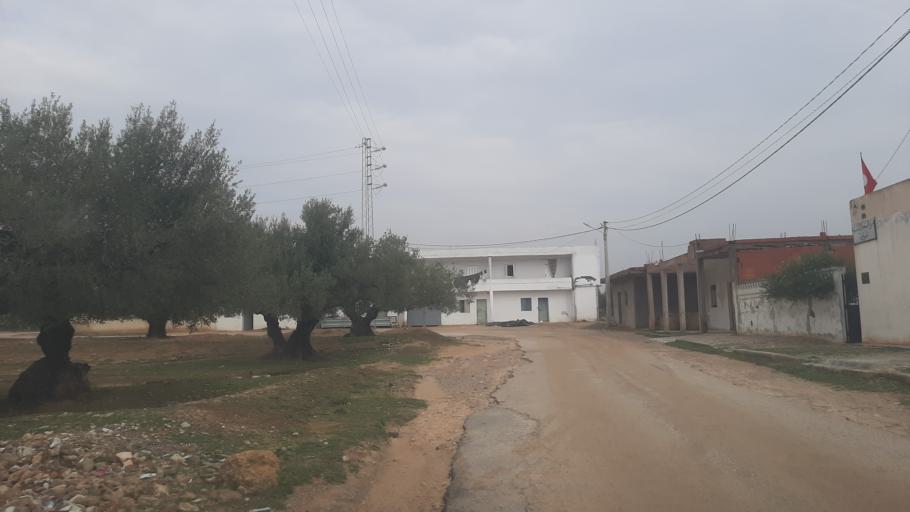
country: TN
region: Al Munastir
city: Sidi Bin Nur
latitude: 35.4823
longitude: 10.8722
